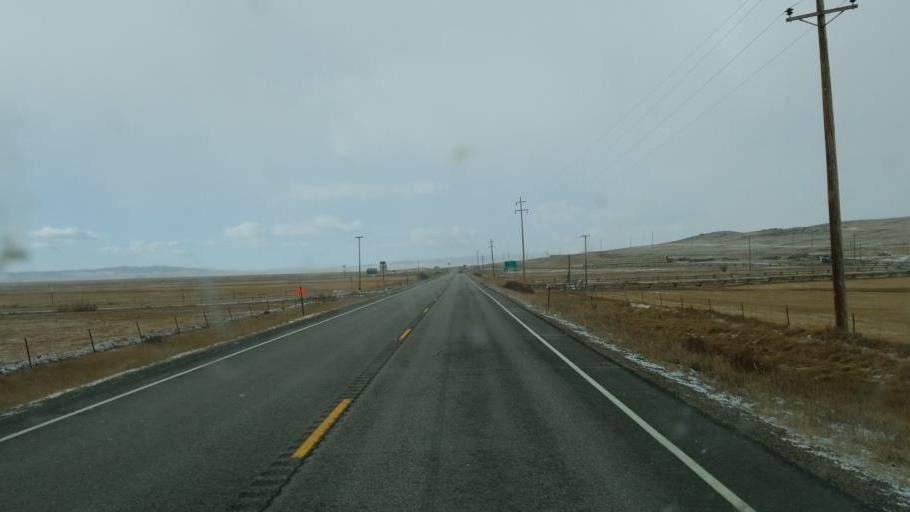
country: US
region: Colorado
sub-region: Summit County
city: Breckenridge
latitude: 39.3925
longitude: -105.7864
